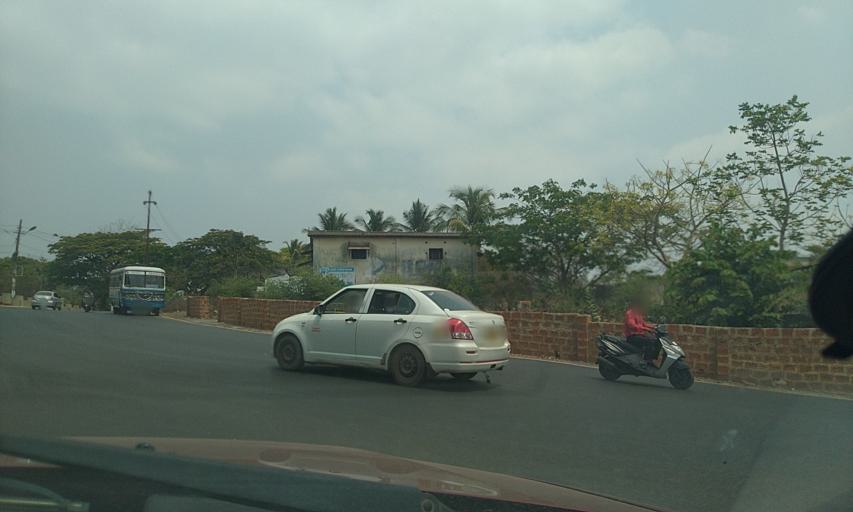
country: IN
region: Goa
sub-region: North Goa
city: Mapuca
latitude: 15.5973
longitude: 73.8099
